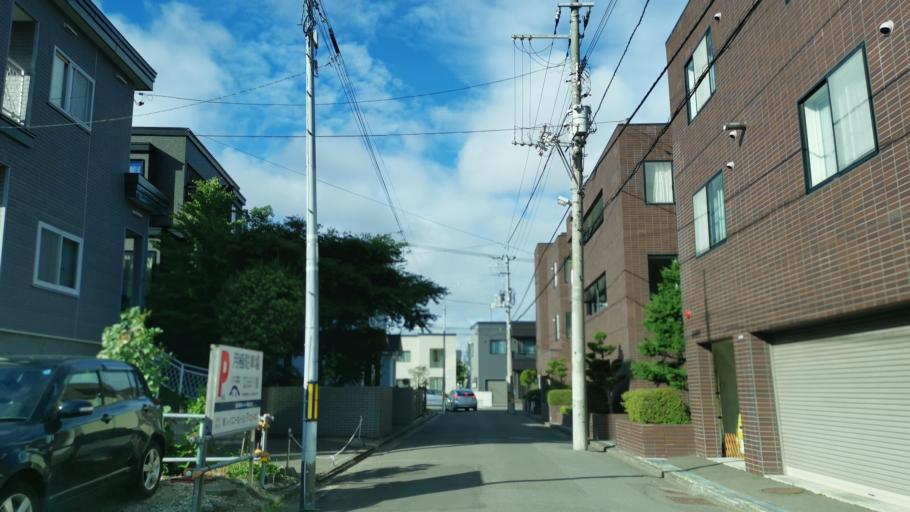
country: JP
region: Hokkaido
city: Sapporo
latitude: 43.0669
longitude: 141.2999
